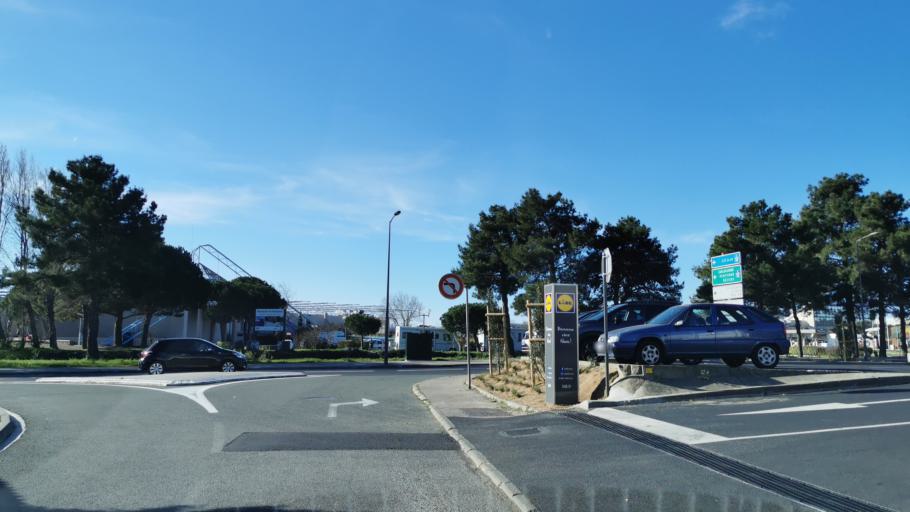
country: FR
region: Languedoc-Roussillon
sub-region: Departement de l'Aude
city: Narbonne
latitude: 43.1758
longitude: 2.9949
